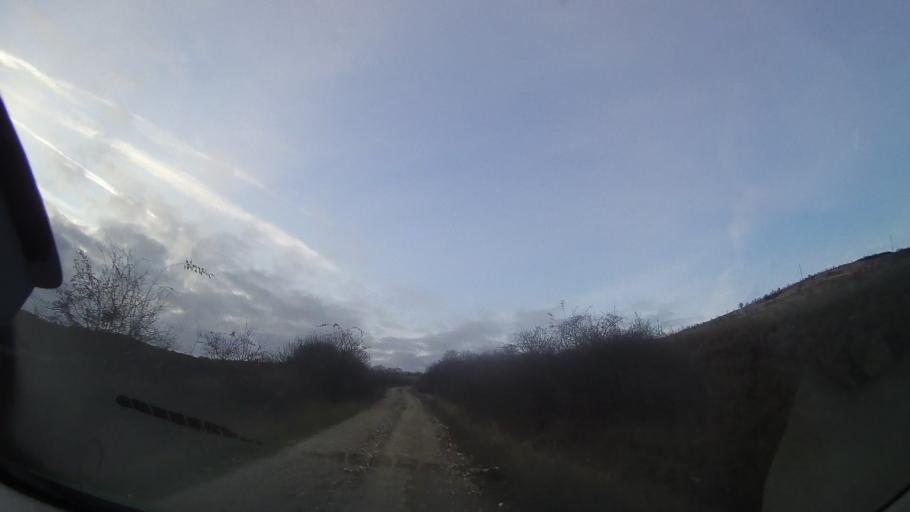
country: RO
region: Cluj
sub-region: Comuna Palatca
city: Palatca
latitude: 46.8581
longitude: 24.0301
